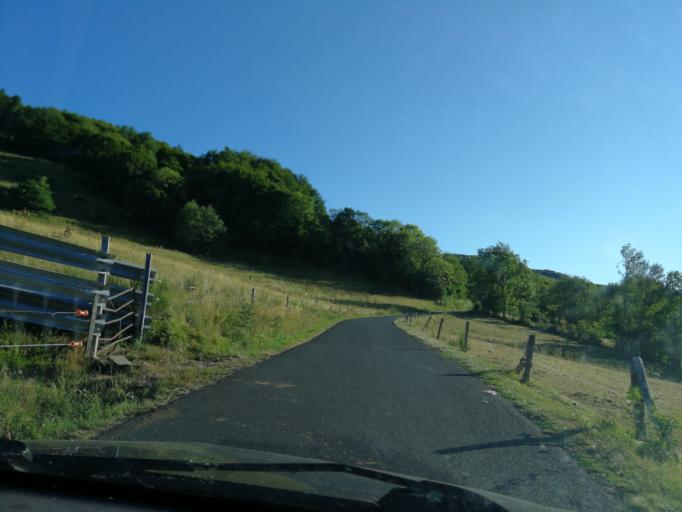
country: FR
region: Auvergne
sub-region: Departement du Cantal
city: Vic-sur-Cere
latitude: 45.0875
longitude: 2.5725
